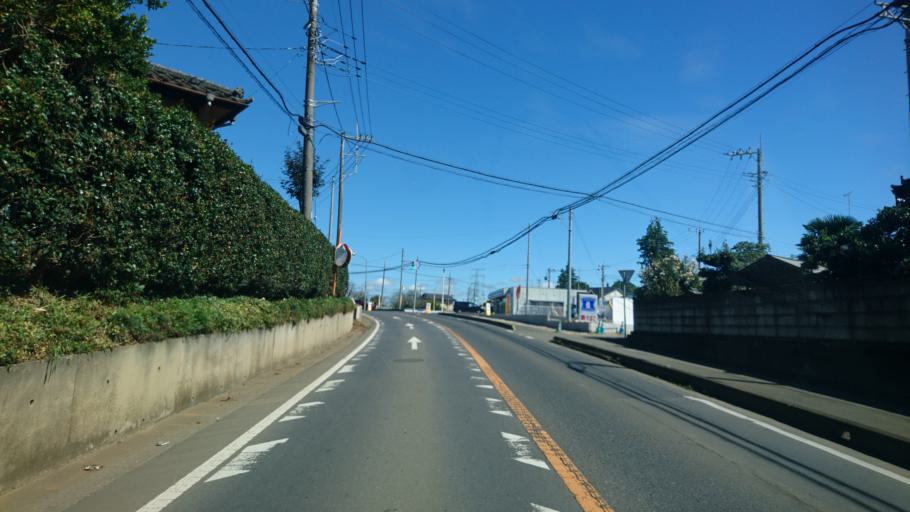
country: JP
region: Ibaraki
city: Ishige
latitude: 36.1526
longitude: 139.8953
